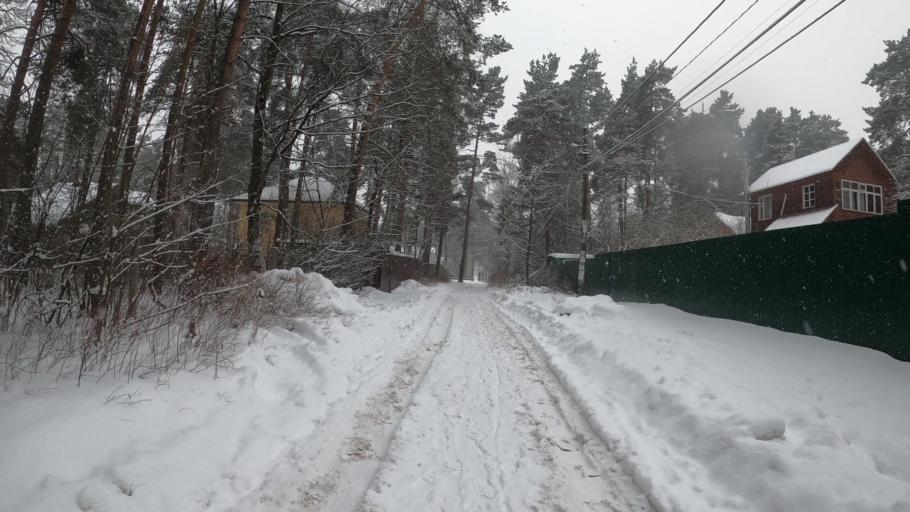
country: RU
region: Moskovskaya
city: Kratovo
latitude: 55.5892
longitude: 38.1627
